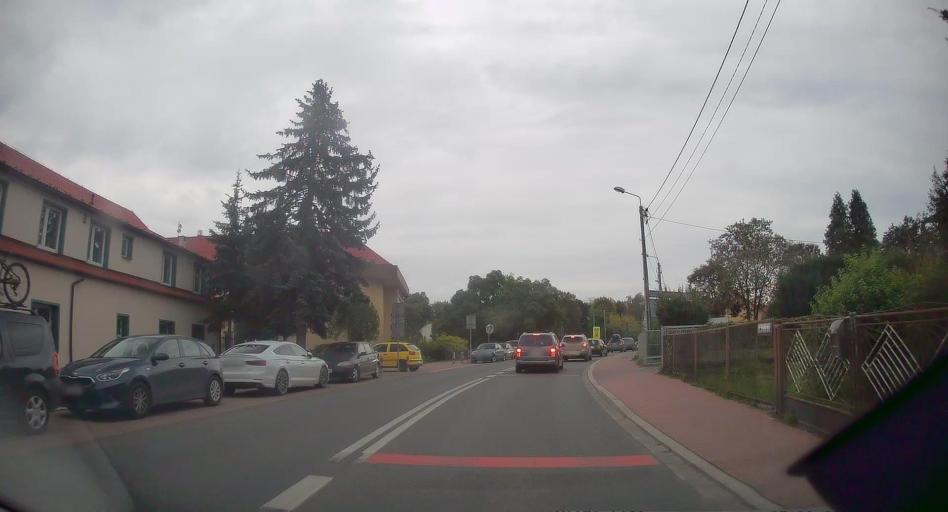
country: PL
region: Lesser Poland Voivodeship
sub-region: Powiat wielicki
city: Niepolomice
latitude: 50.0359
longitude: 20.2153
